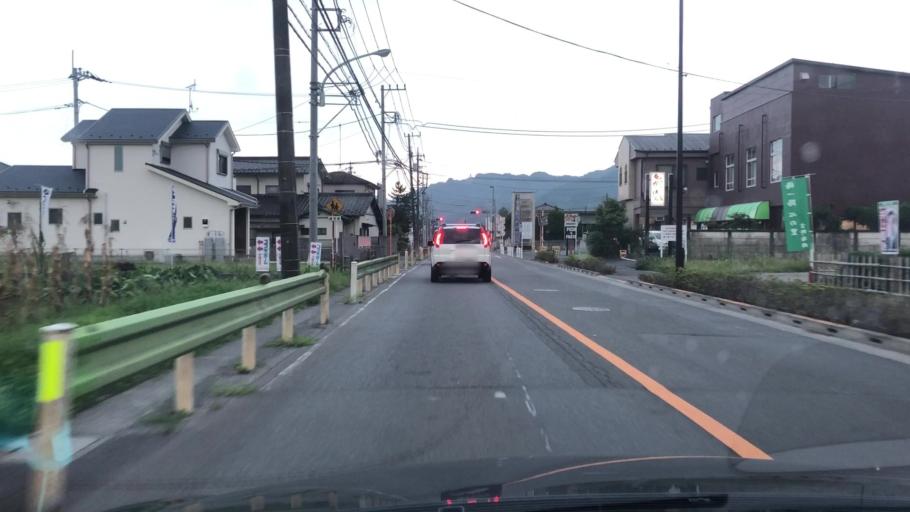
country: JP
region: Tokyo
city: Ome
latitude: 35.7891
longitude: 139.2217
